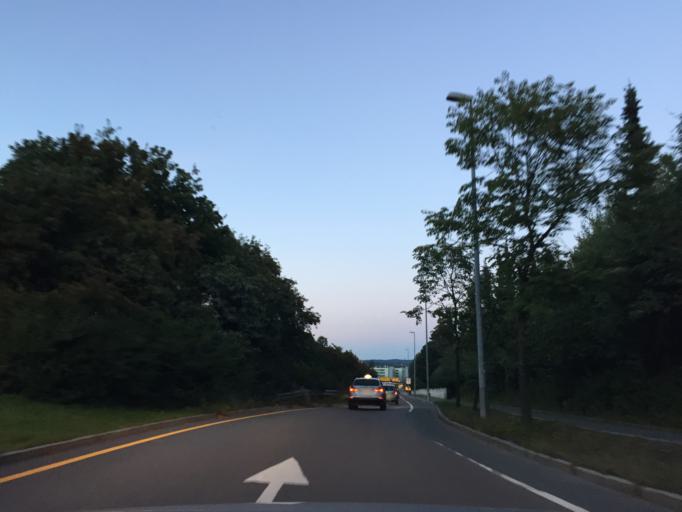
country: NO
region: Akershus
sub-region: Baerum
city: Lysaker
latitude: 59.9256
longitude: 10.6493
